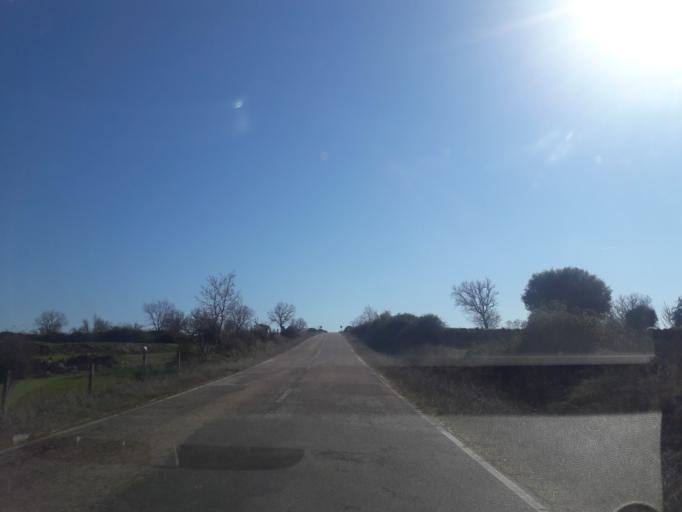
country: ES
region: Castille and Leon
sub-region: Provincia de Salamanca
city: Cabeza del Caballo
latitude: 41.1629
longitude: -6.5461
